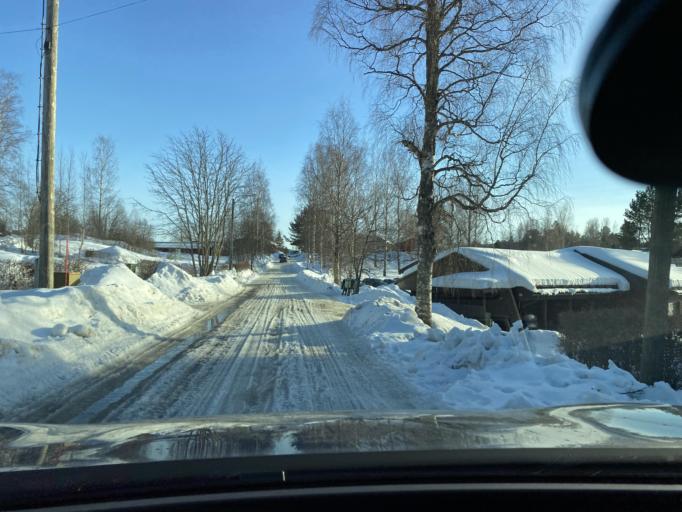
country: FI
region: Central Finland
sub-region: Jyvaeskylae
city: Korpilahti
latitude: 62.0172
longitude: 25.5688
